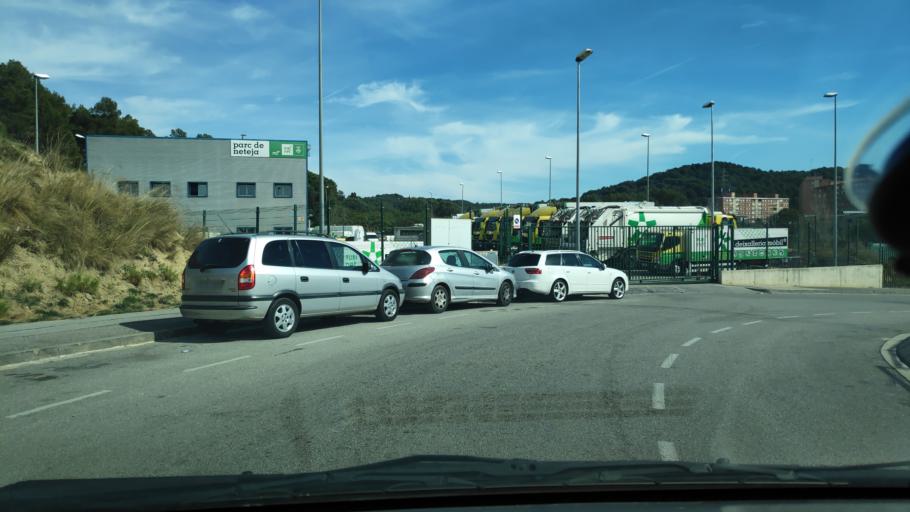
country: ES
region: Catalonia
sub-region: Provincia de Barcelona
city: Rubi
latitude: 41.5104
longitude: 2.0428
